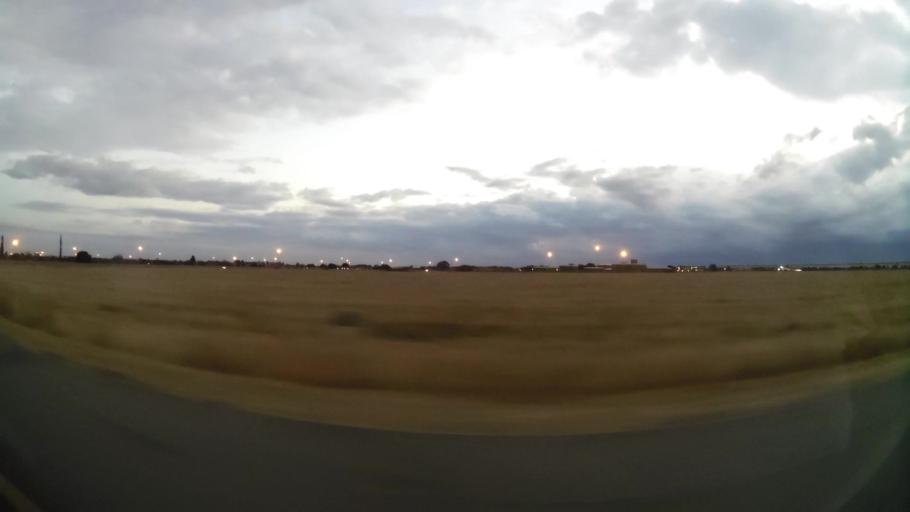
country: ZA
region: Orange Free State
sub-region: Lejweleputswa District Municipality
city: Welkom
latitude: -27.9475
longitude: 26.7954
